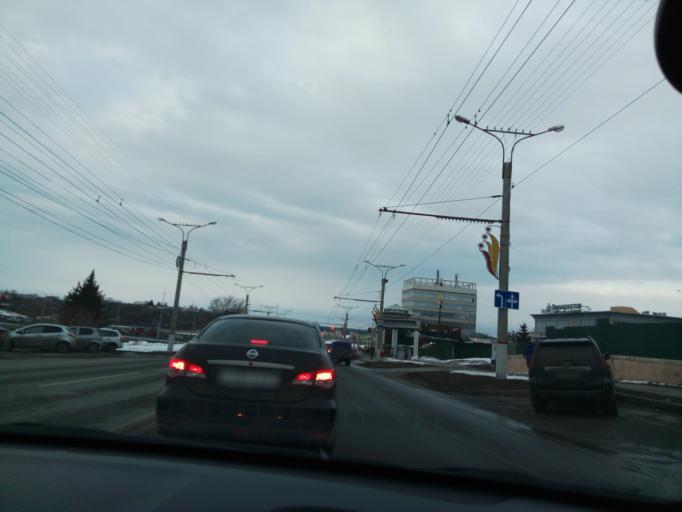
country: RU
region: Chuvashia
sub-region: Cheboksarskiy Rayon
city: Cheboksary
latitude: 56.1425
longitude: 47.2455
